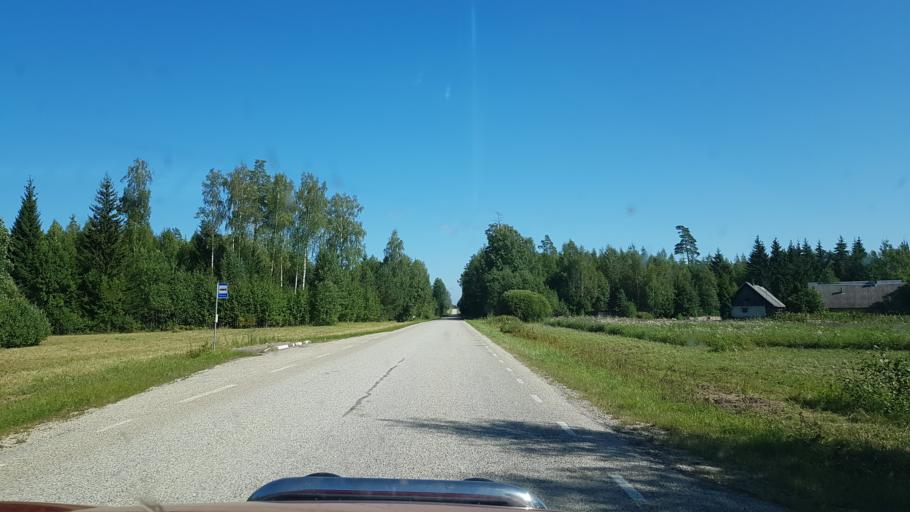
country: EE
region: Polvamaa
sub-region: Raepina vald
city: Rapina
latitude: 58.2239
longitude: 27.2904
